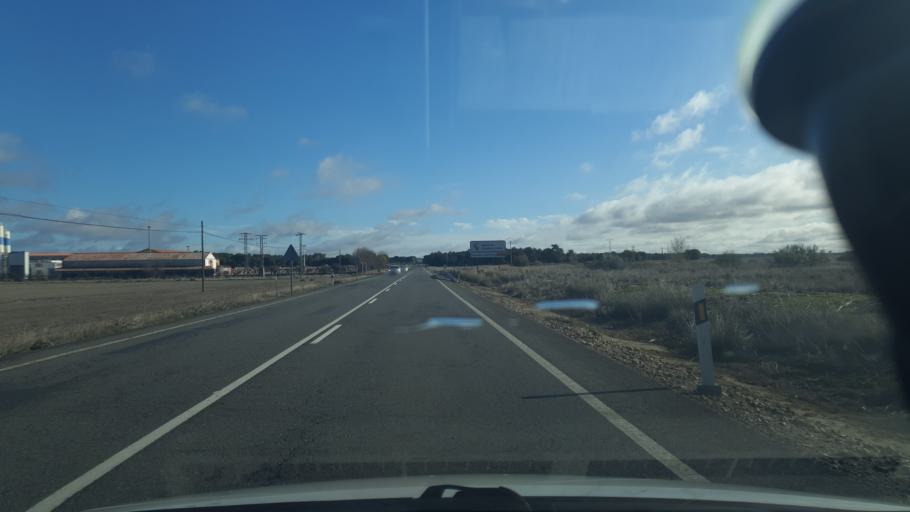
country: ES
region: Castille and Leon
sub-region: Provincia de Segovia
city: Martin Munoz de la Dehesa
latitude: 41.0459
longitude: -4.6793
